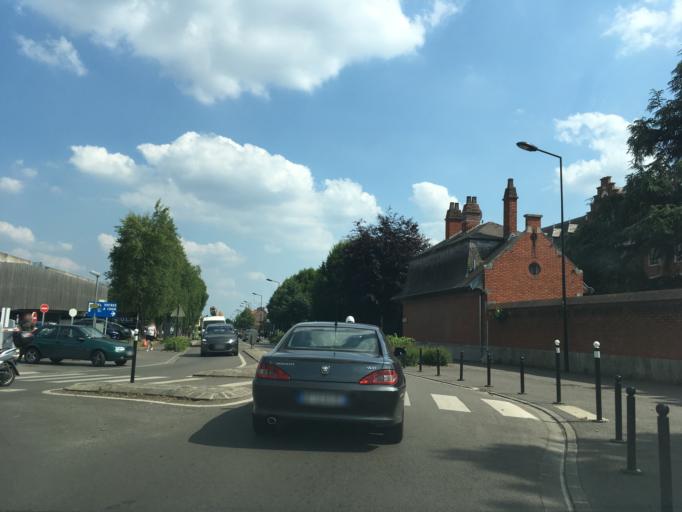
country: FR
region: Nord-Pas-de-Calais
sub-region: Departement du Nord
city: Anzin
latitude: 50.3593
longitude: 3.5000
